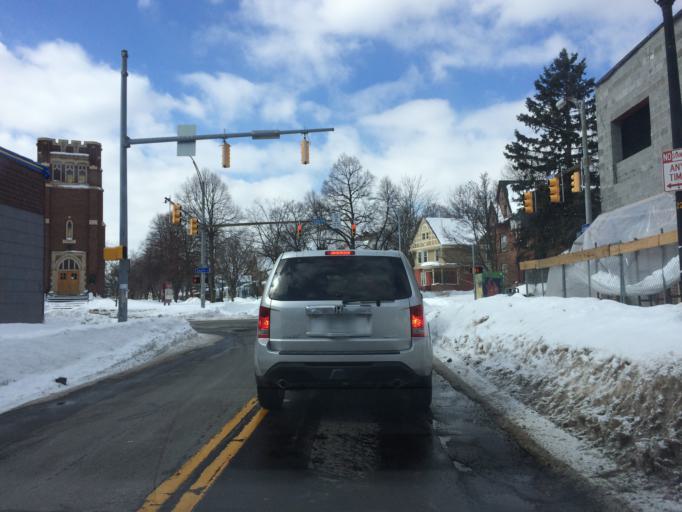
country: US
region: New York
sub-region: Monroe County
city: Rochester
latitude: 43.1387
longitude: -77.6056
